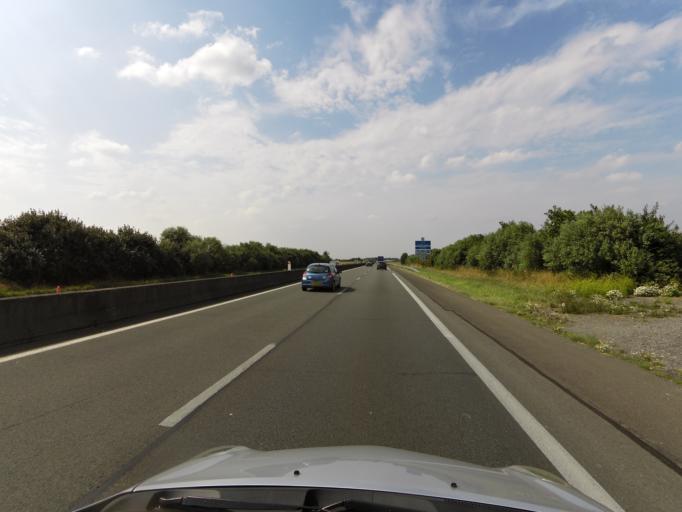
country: FR
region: Picardie
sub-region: Departement de l'Aisne
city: Itancourt
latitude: 49.7743
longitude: 3.3477
